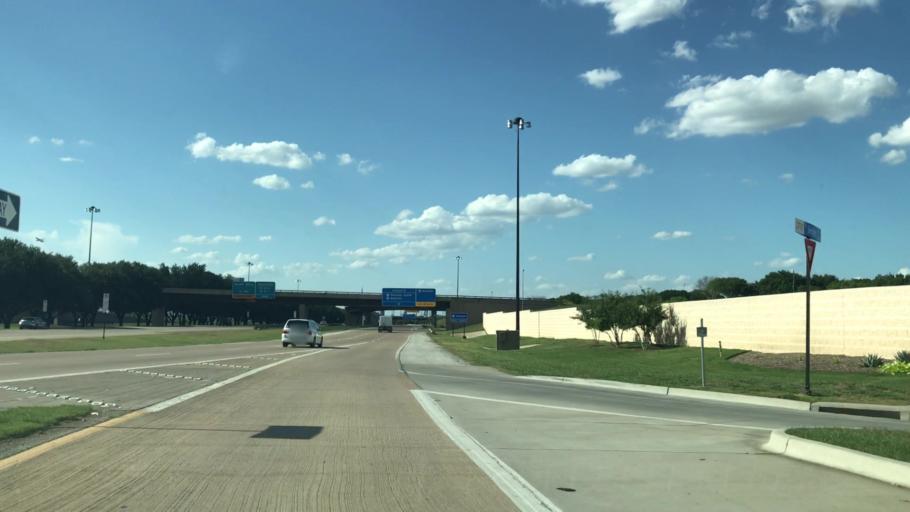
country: US
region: Texas
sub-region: Tarrant County
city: Euless
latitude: 32.8556
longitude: -97.0400
